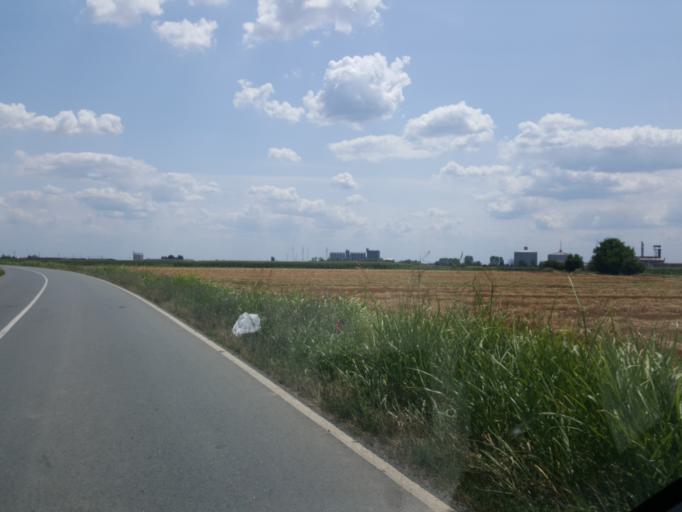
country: RS
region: Autonomna Pokrajina Vojvodina
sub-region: Sremski Okrug
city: Pecinci
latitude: 44.9011
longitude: 19.9574
